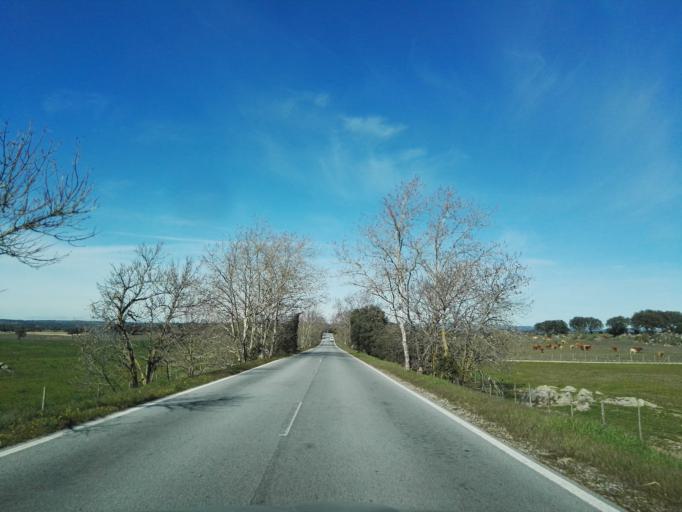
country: PT
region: Portalegre
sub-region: Arronches
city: Arronches
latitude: 39.0399
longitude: -7.2596
